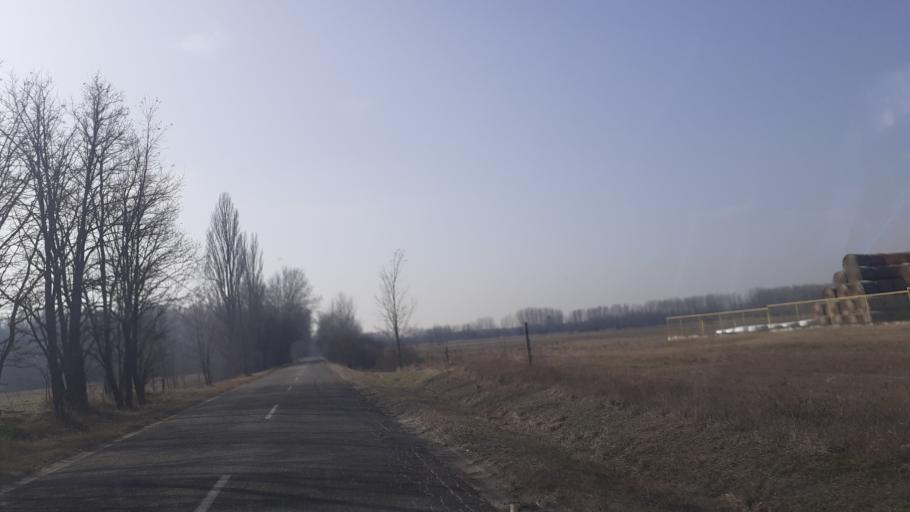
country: HU
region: Pest
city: Orkeny
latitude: 47.0657
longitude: 19.3491
